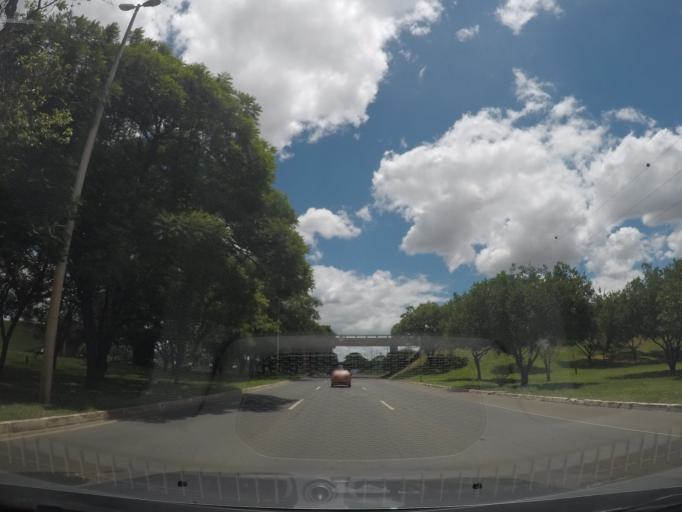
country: BR
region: Federal District
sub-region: Brasilia
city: Brasilia
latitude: -15.8073
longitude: -47.9482
